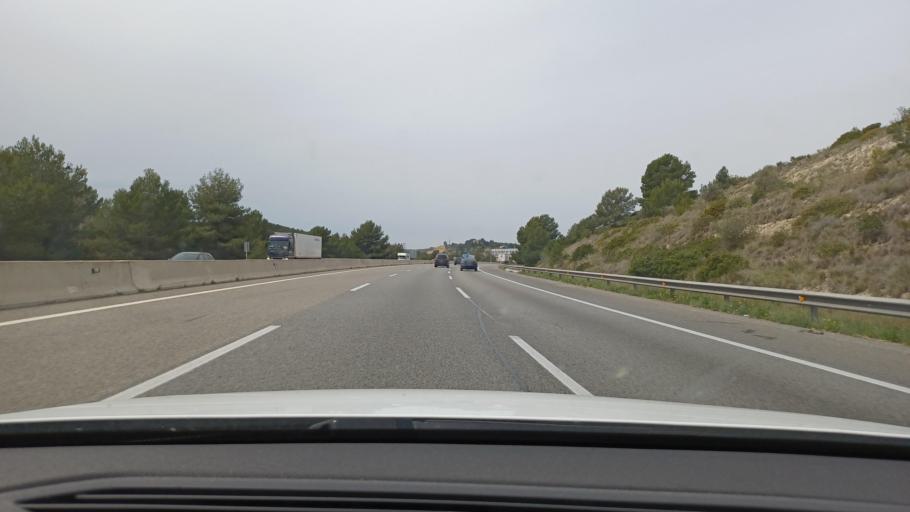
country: ES
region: Catalonia
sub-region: Provincia de Tarragona
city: Altafulla
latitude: 41.1573
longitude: 1.3829
